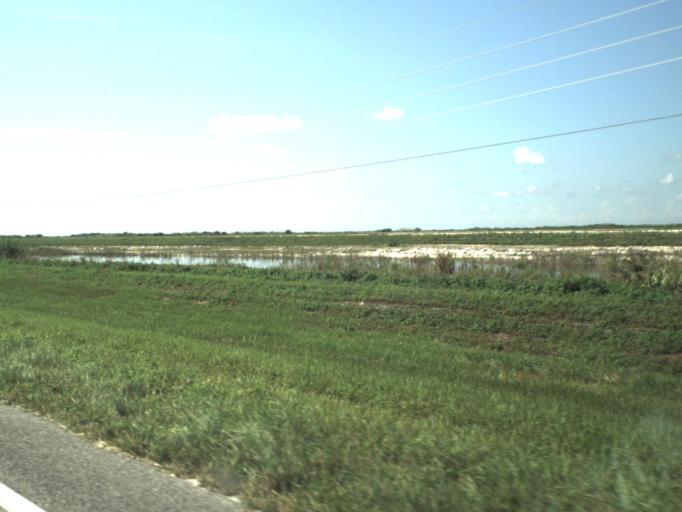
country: US
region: Florida
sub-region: Palm Beach County
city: Belle Glade Camp
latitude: 26.4491
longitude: -80.6264
